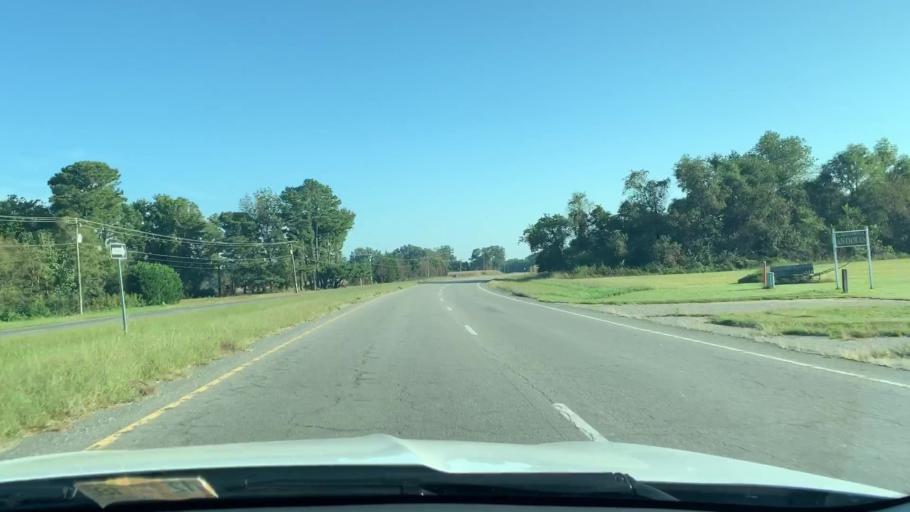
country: US
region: Virginia
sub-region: Lancaster County
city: Kilmarnock
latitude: 37.6675
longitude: -76.3819
